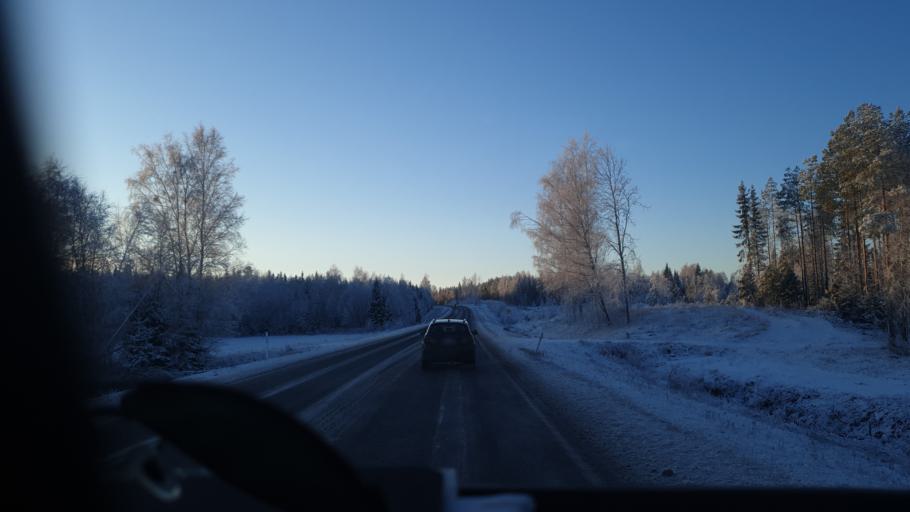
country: FI
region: Central Ostrobothnia
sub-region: Kokkola
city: Kaelviae
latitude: 63.9096
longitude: 23.3925
